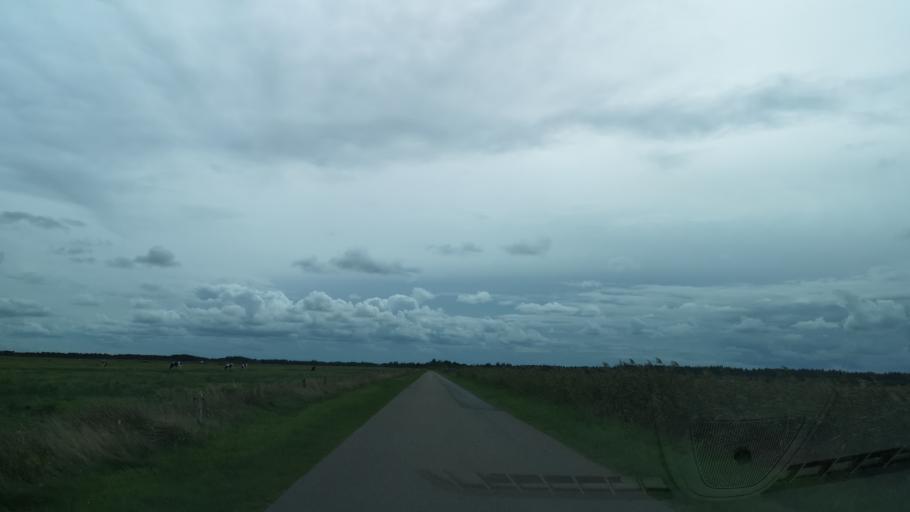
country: DK
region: Central Jutland
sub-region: Ringkobing-Skjern Kommune
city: Hvide Sande
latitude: 55.8407
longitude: 8.2174
